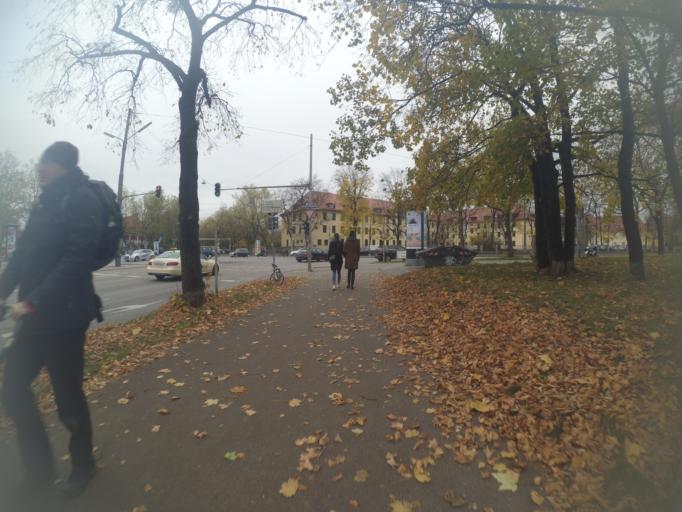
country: DE
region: Bavaria
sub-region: Upper Bavaria
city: Munich
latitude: 48.1619
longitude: 11.5527
